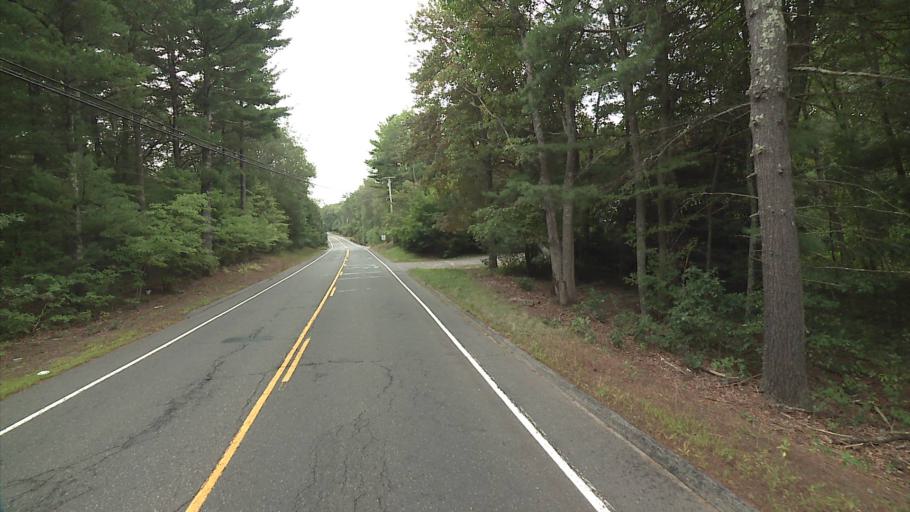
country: US
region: Connecticut
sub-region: Tolland County
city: Storrs
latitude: 41.8838
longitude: -72.2679
